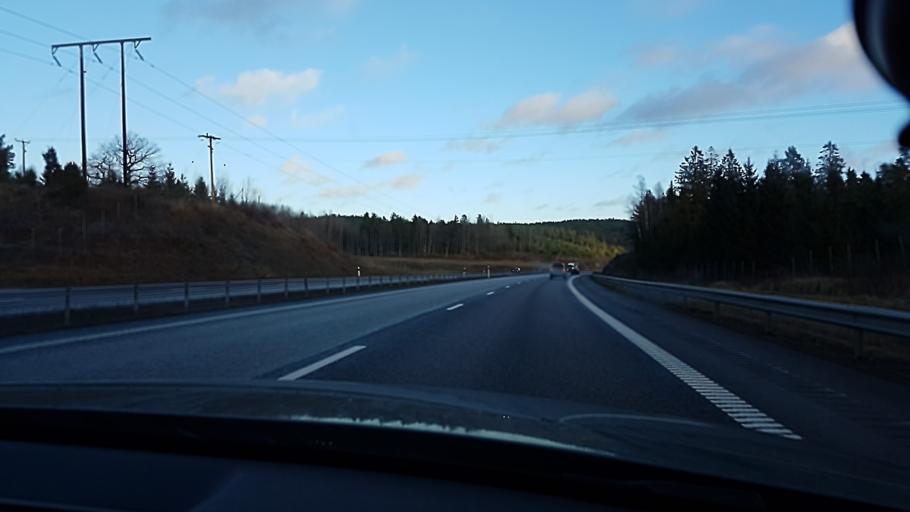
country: SE
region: OEstergoetland
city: Lindo
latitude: 58.6764
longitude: 16.2627
